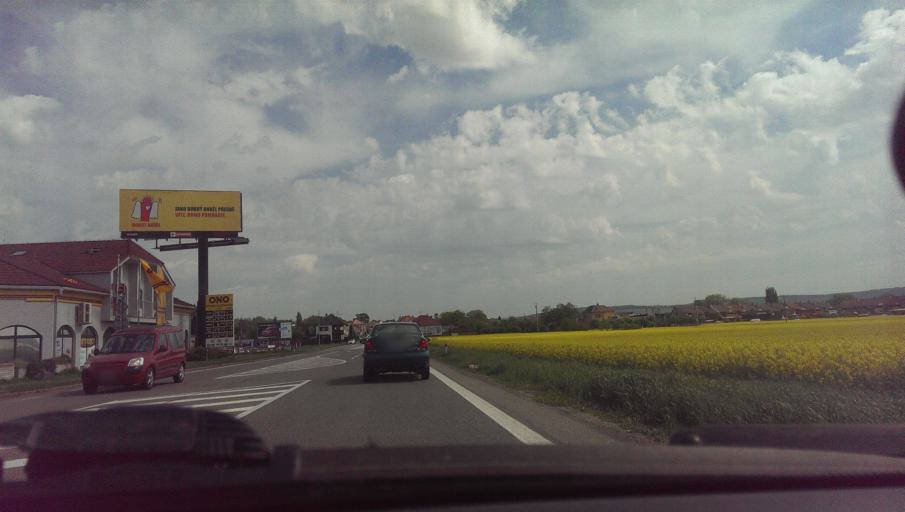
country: CZ
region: Zlin
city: Spytihnev
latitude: 49.1342
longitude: 17.4878
